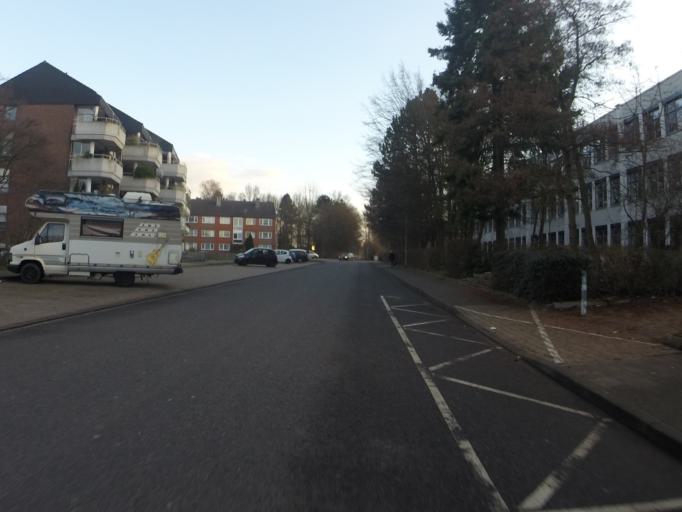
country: NL
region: Limburg
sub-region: Gemeente Kerkrade
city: Kerkrade
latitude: 50.8276
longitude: 6.0865
